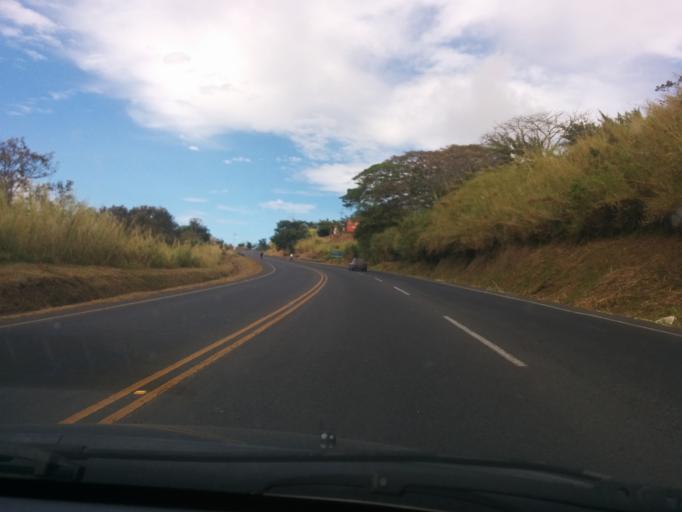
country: CR
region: Alajuela
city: San Ramon
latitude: 10.0791
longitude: -84.4646
